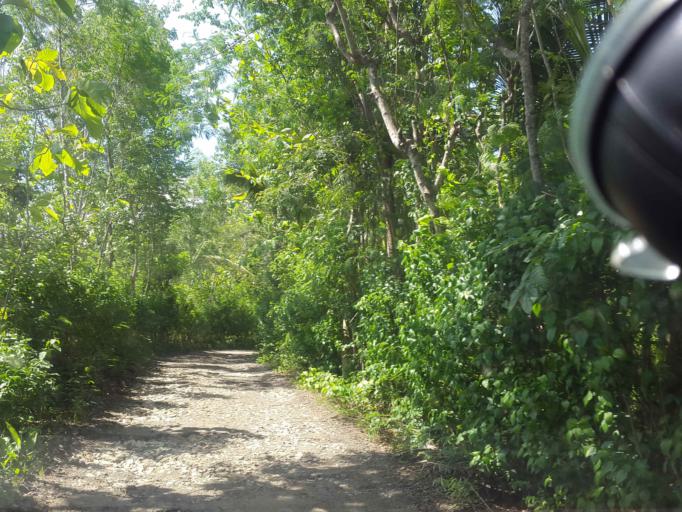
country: ID
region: East Java
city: Ngares
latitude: -8.0152
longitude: 111.6915
